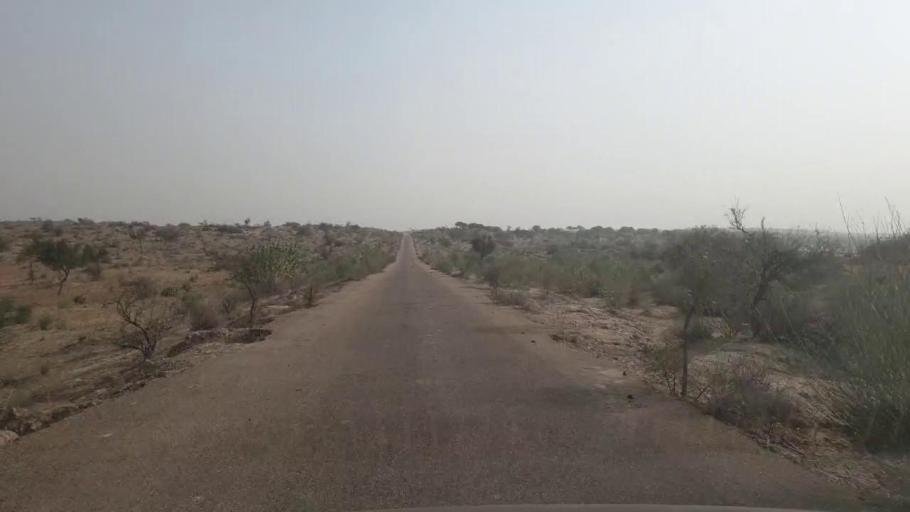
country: PK
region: Sindh
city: Chor
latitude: 25.5039
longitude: 69.9696
